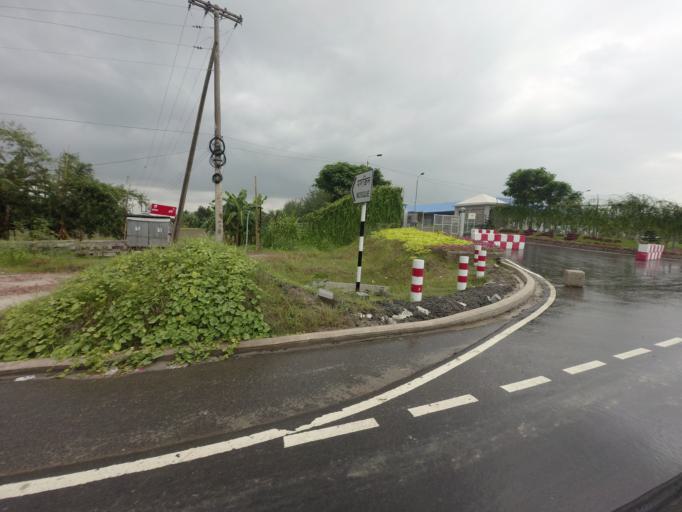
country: BD
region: Dhaka
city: Char Bhadrasan
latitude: 23.3995
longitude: 90.2170
